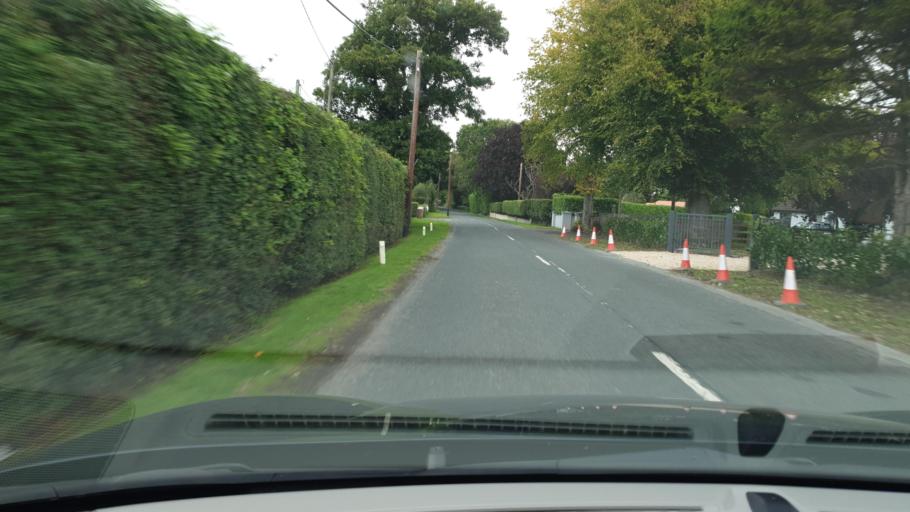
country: IE
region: Leinster
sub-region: Kildare
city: Clane
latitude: 53.3194
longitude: -6.6388
